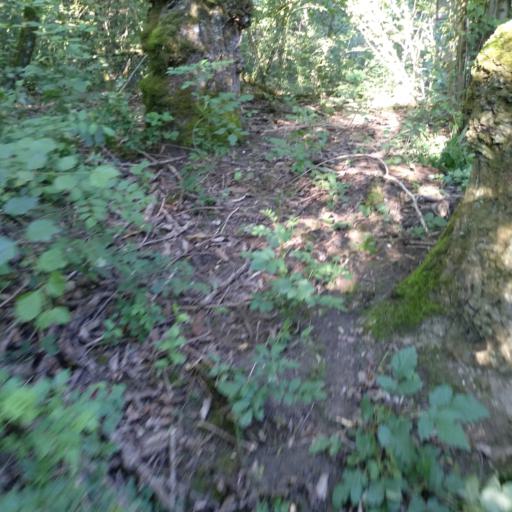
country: FR
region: Rhone-Alpes
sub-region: Departement de l'Ain
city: Miribel
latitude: 45.8010
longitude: 4.9671
